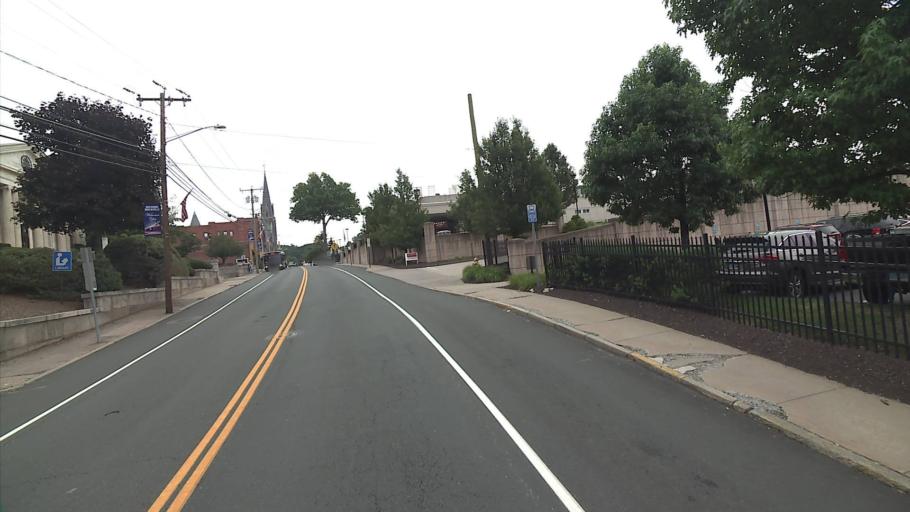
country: US
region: Connecticut
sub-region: Tolland County
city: Rockville
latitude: 41.8669
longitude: -72.4521
